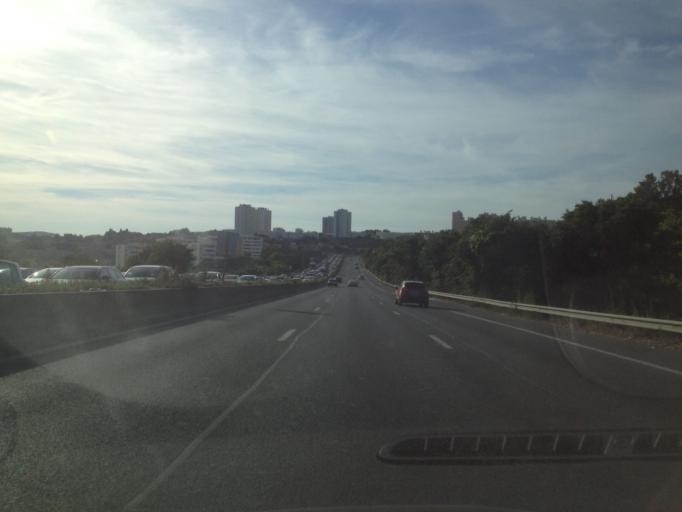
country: FR
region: Provence-Alpes-Cote d'Azur
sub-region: Departement des Bouches-du-Rhone
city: Marseille 14
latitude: 43.3484
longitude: 5.3706
